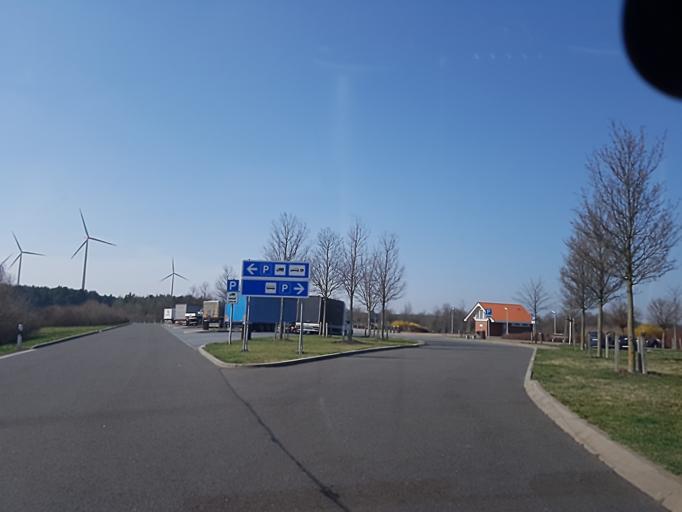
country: DE
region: Brandenburg
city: Vetschau
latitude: 51.7550
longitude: 14.1279
